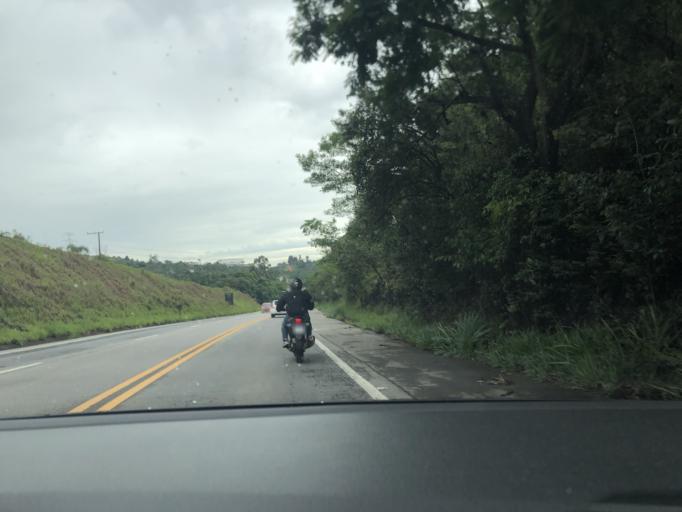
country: BR
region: Sao Paulo
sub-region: Jarinu
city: Jarinu
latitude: -23.1412
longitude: -46.7429
